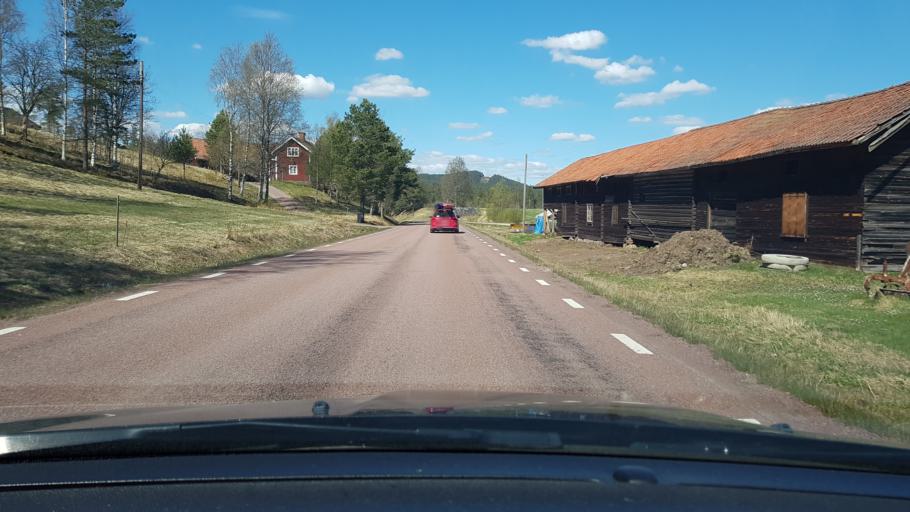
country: SE
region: Dalarna
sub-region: Alvdalens Kommun
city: AElvdalen
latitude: 61.1178
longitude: 14.1591
